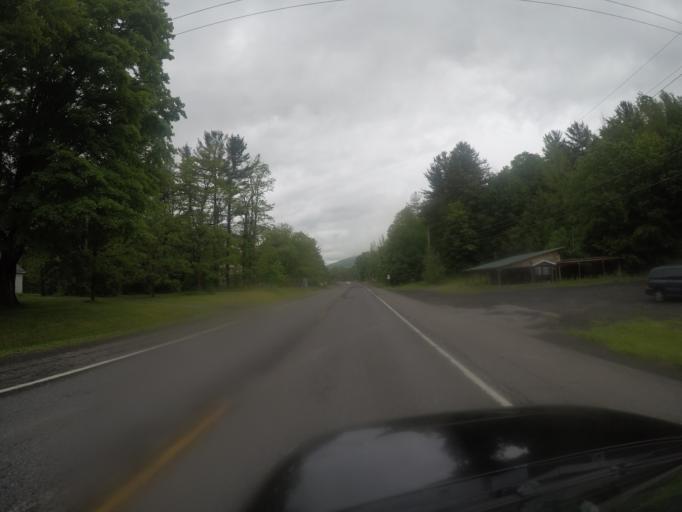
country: US
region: New York
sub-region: Ulster County
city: Shokan
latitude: 42.0367
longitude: -74.2773
